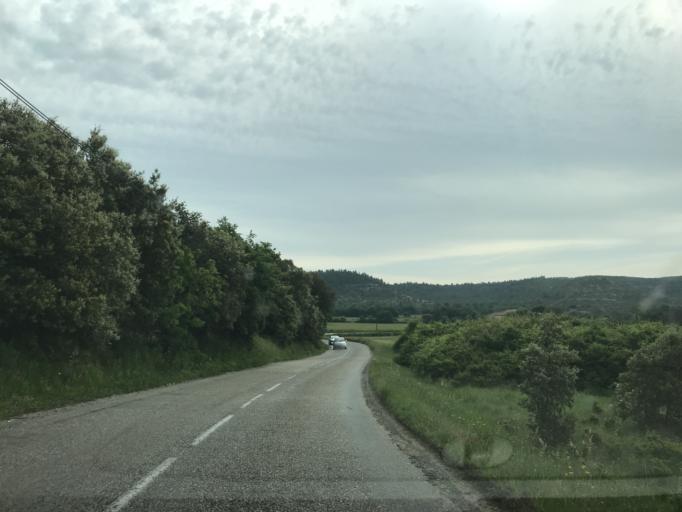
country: FR
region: Provence-Alpes-Cote d'Azur
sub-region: Departement du Vaucluse
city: Beaumont-de-Pertuis
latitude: 43.6780
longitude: 5.7235
